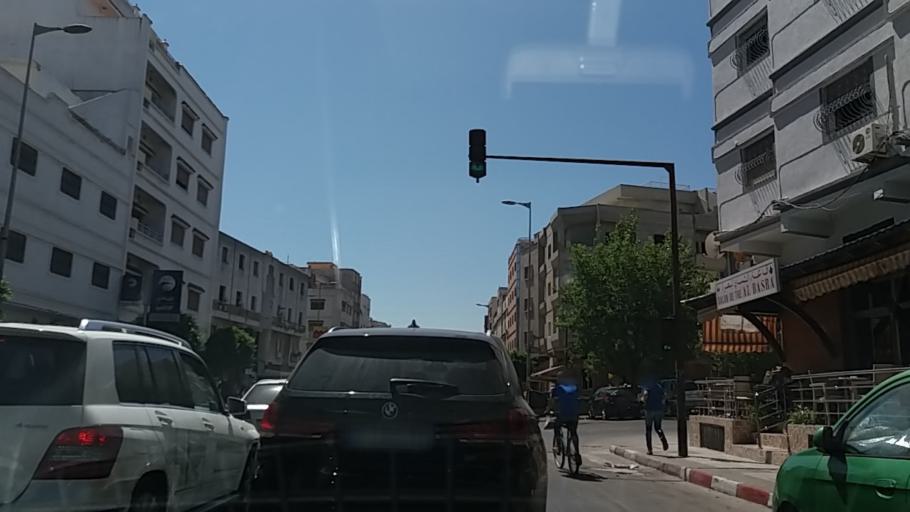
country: MA
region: Tanger-Tetouan
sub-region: Tanger-Assilah
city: Tangier
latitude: 35.7604
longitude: -5.8024
